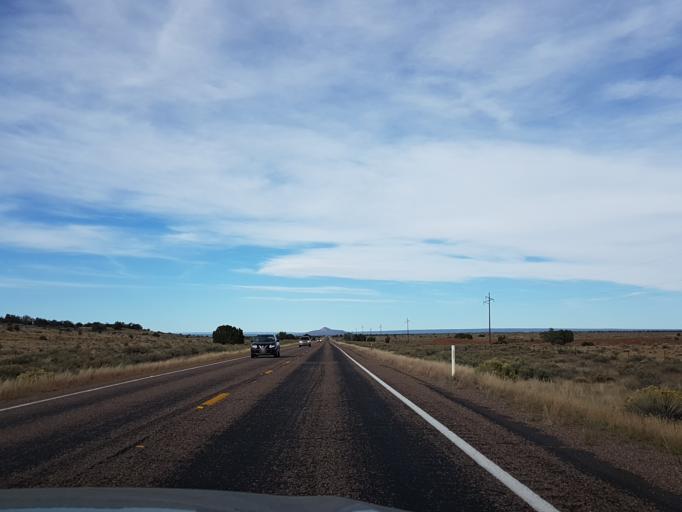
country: US
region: Arizona
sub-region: Coconino County
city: Williams
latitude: 35.5681
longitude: -112.1557
